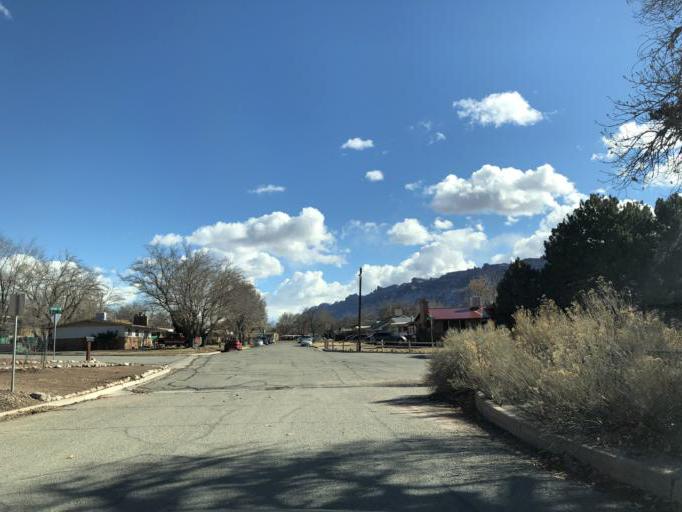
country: US
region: Utah
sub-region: Grand County
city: Moab
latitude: 38.5706
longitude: -109.5379
